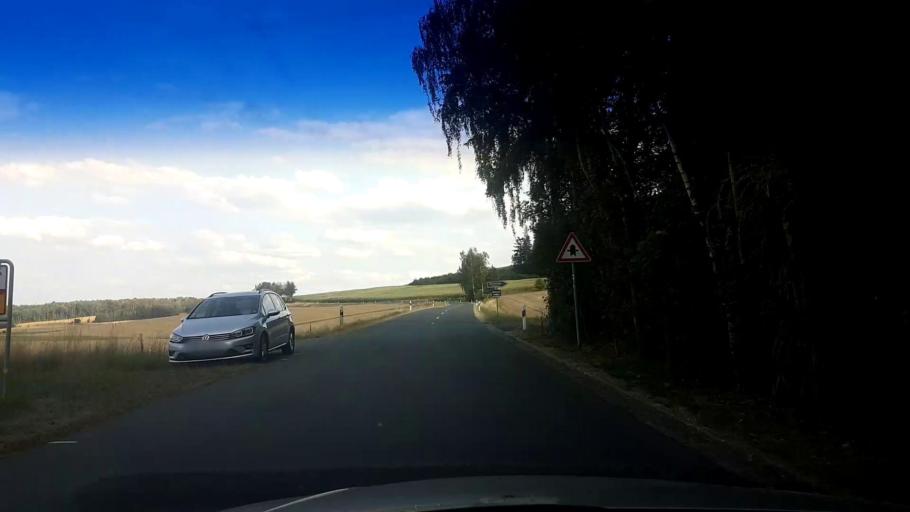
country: DE
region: Bavaria
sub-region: Upper Palatinate
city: Waldsassen
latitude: 50.0227
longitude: 12.3456
